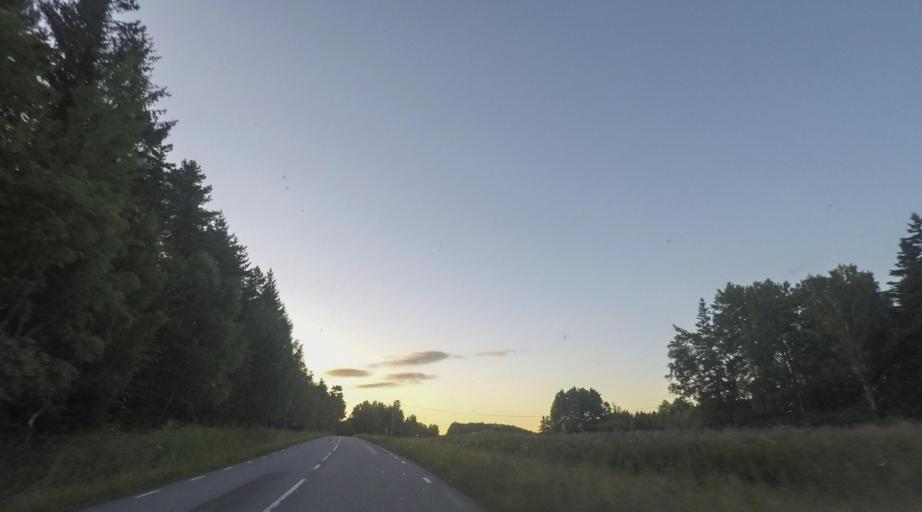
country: SE
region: Soedermanland
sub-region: Trosa Kommun
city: Trosa
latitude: 58.9722
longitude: 17.6940
